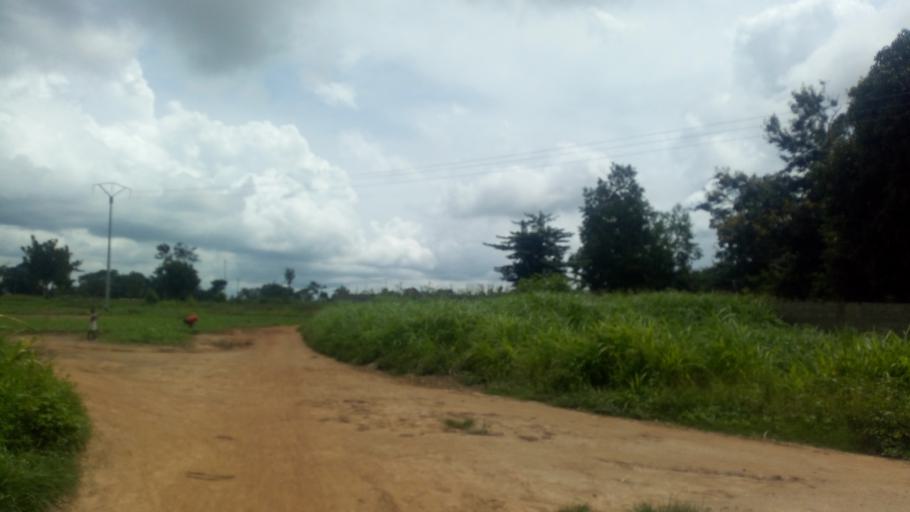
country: TG
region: Centrale
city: Sotouboua
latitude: 8.5563
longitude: 0.9958
